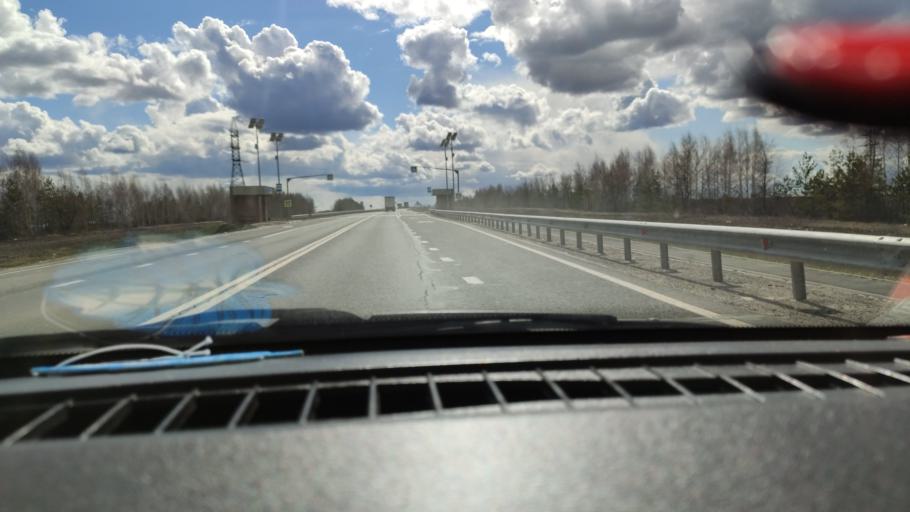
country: RU
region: Saratov
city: Dukhovnitskoye
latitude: 52.8380
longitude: 48.2439
